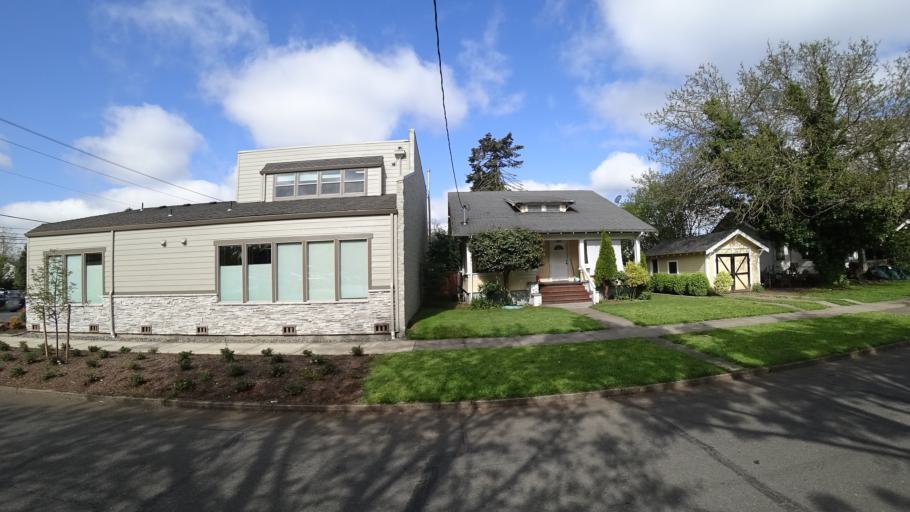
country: US
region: Oregon
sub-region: Washington County
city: Hillsboro
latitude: 45.5190
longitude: -122.9809
